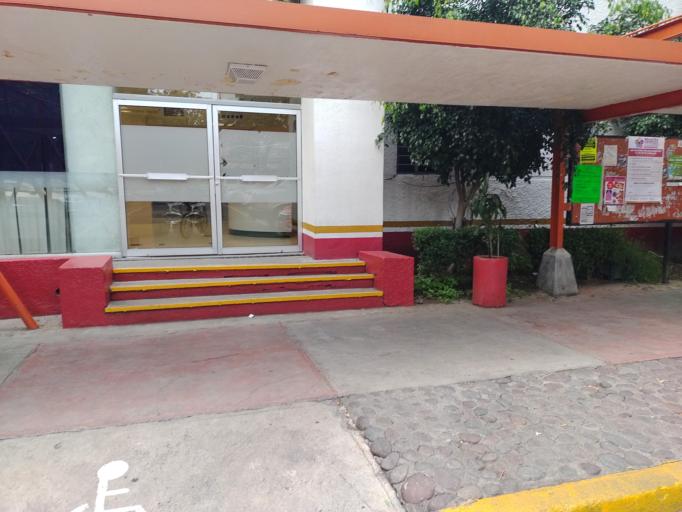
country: MX
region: Mexico City
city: Cuauhtemoc
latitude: 19.4546
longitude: -99.1462
